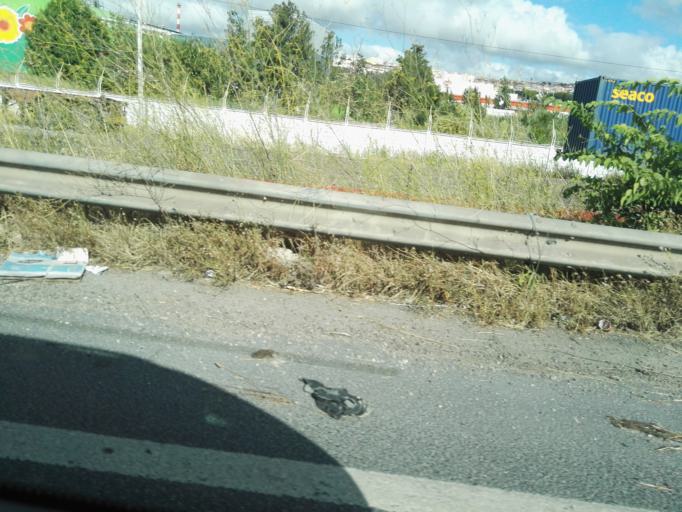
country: PT
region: Lisbon
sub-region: Loures
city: Santa Iria da Azoia
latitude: 38.8332
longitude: -9.0777
